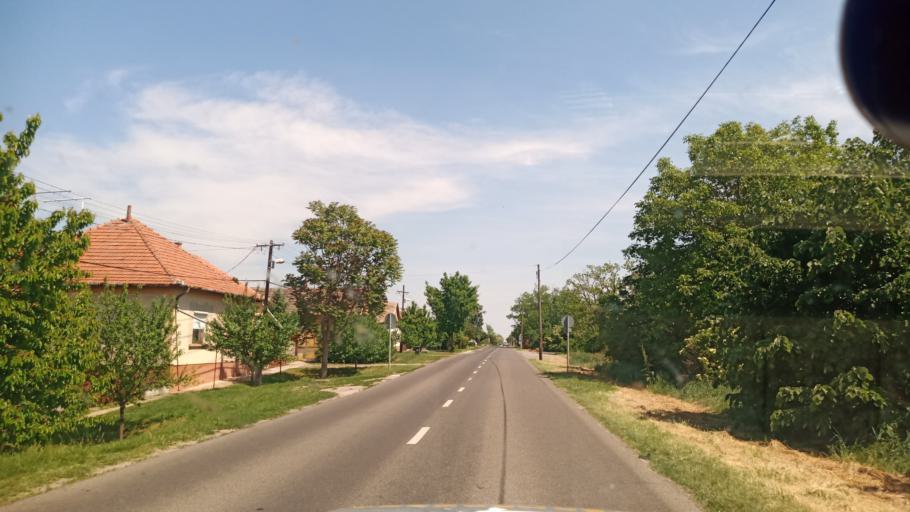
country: HU
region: Bekes
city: Oroshaza
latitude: 46.5663
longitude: 20.5920
